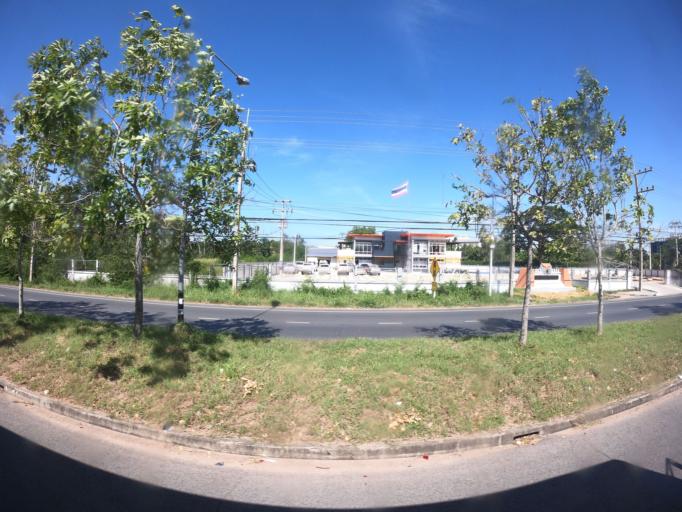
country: TH
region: Nakhon Ratchasima
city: Nakhon Ratchasima
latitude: 15.0002
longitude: 102.1179
